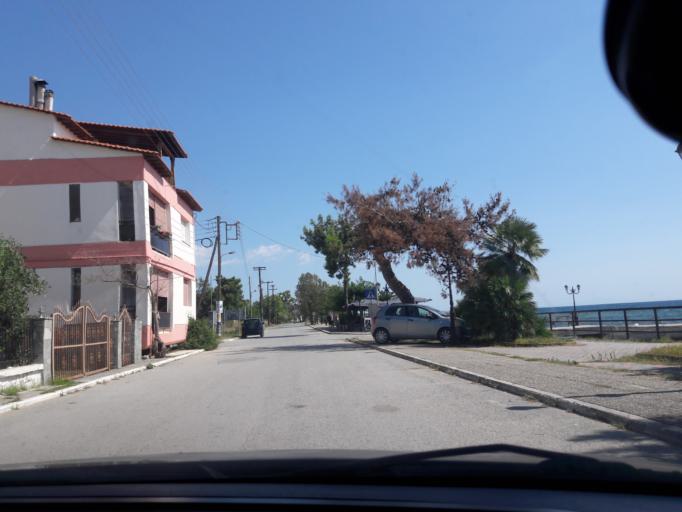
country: GR
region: Central Macedonia
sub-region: Nomos Chalkidikis
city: Nea Kallikrateia
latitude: 40.3442
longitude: 23.0144
